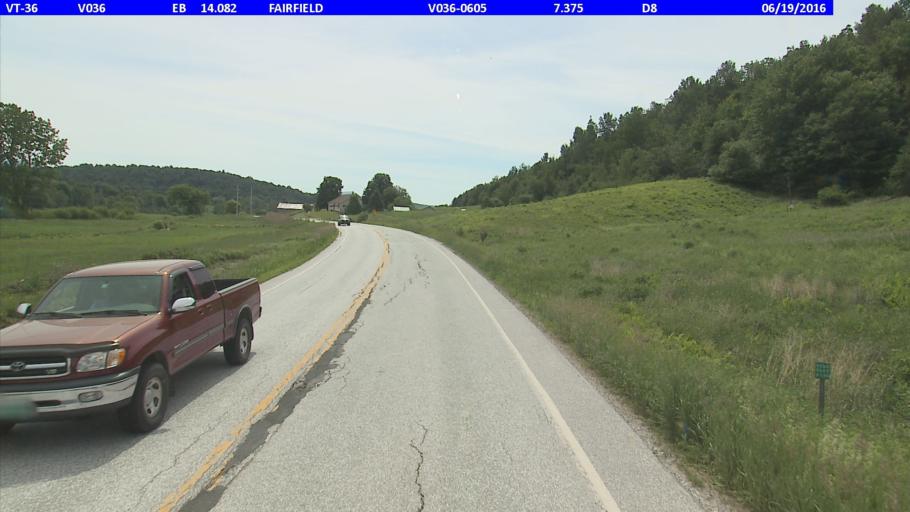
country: US
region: Vermont
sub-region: Franklin County
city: Enosburg Falls
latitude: 44.8001
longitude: -72.8929
